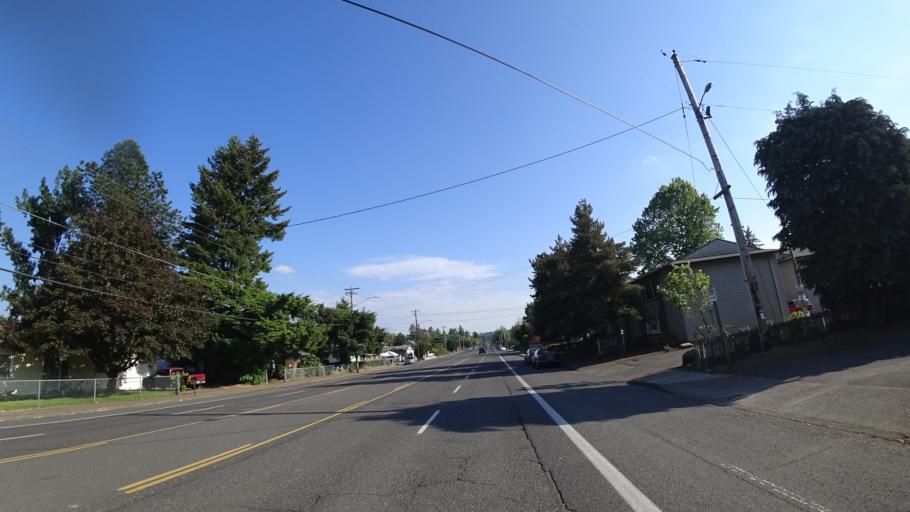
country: US
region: Oregon
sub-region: Multnomah County
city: Fairview
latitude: 45.5159
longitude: -122.4966
